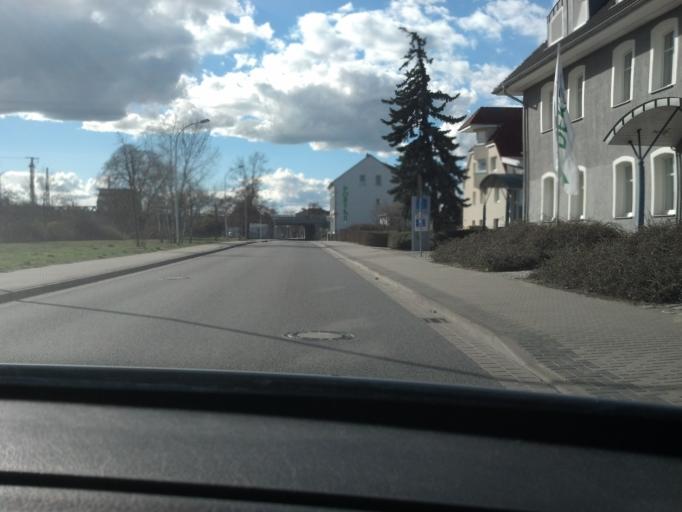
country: DE
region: Mecklenburg-Vorpommern
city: Neubrandenburg
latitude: 53.5615
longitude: 13.2722
